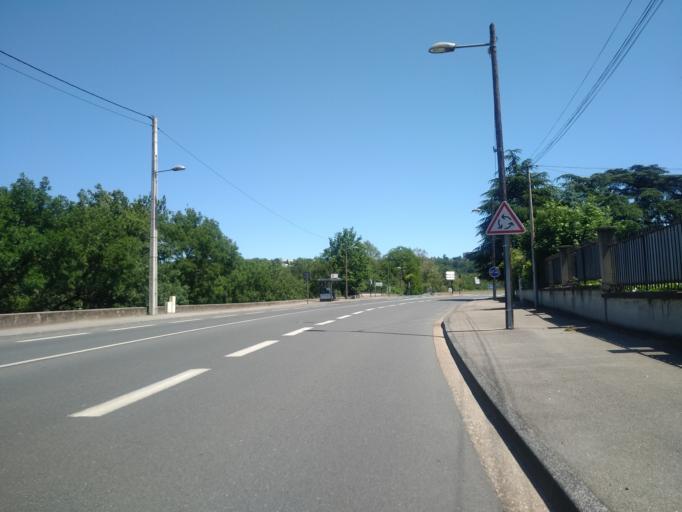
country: FR
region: Rhone-Alpes
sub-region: Departement du Rhone
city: Fontaines-sur-Saone
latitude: 45.8316
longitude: 4.8461
